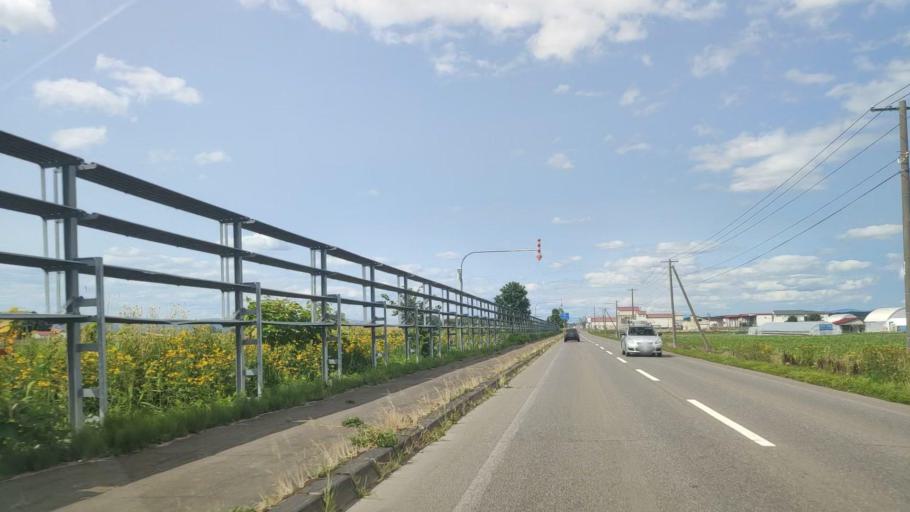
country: JP
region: Hokkaido
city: Nayoro
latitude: 44.1980
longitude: 142.4159
